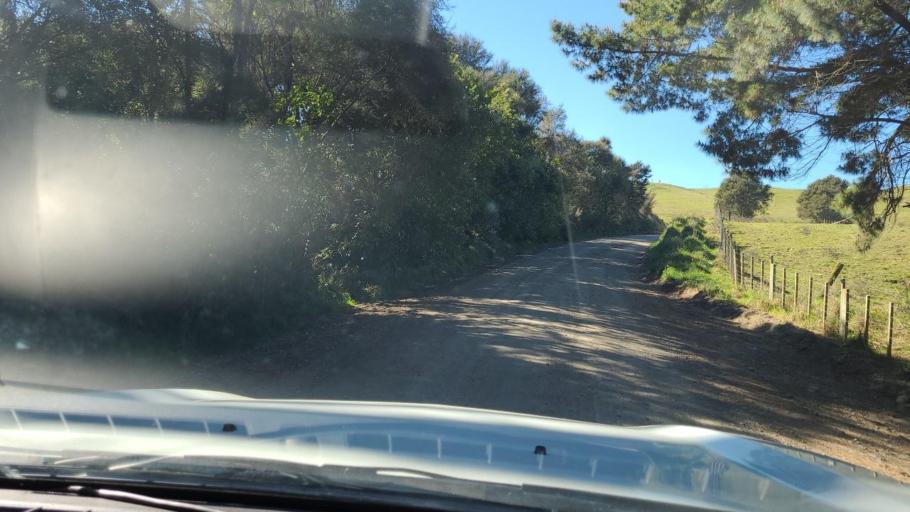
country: NZ
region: Hawke's Bay
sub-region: Napier City
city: Taradale
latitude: -39.4193
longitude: 176.4925
